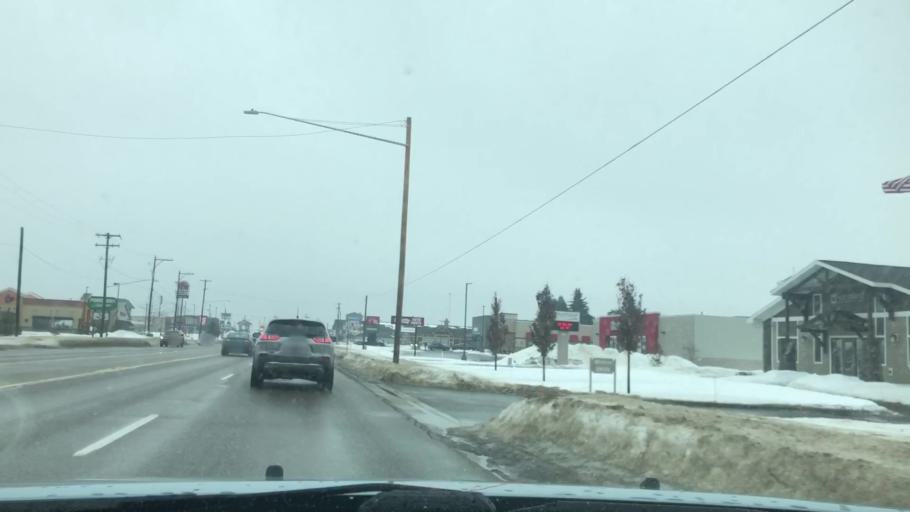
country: US
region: Michigan
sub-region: Otsego County
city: Gaylord
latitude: 45.0274
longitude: -84.6978
